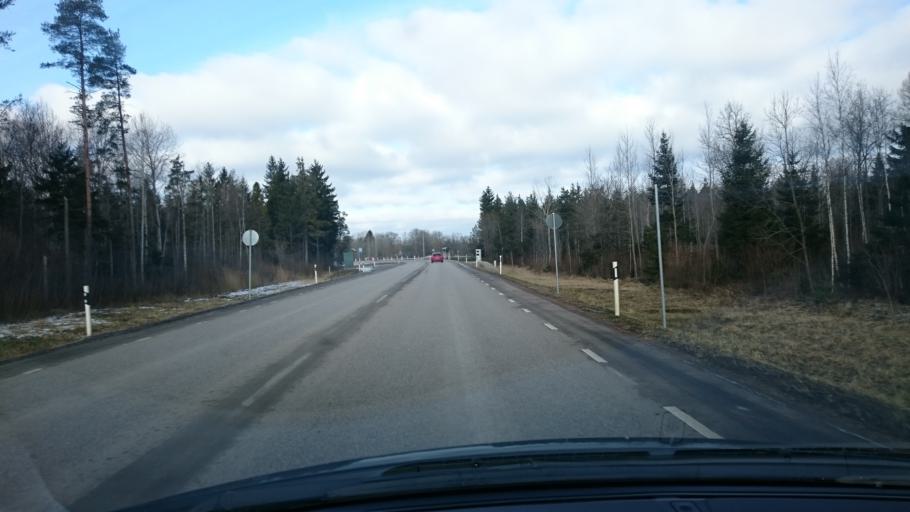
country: EE
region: Harju
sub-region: Saku vald
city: Saku
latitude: 59.3067
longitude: 24.6347
